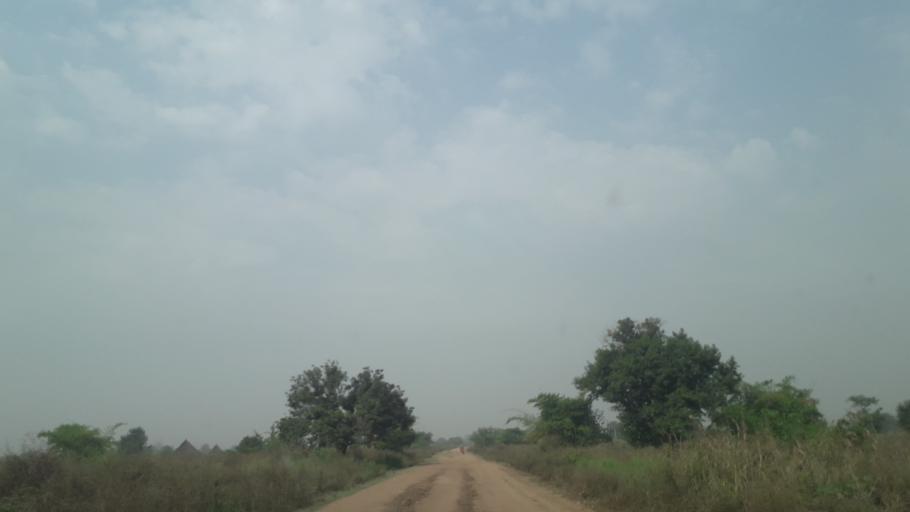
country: ET
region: Gambela
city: Gambela
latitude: 8.3288
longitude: 33.7338
